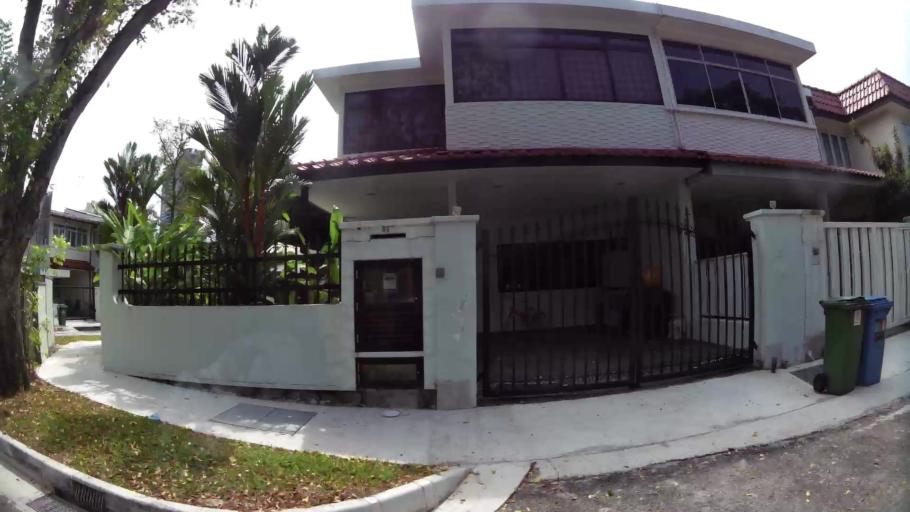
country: SG
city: Singapore
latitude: 1.3195
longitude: 103.7585
